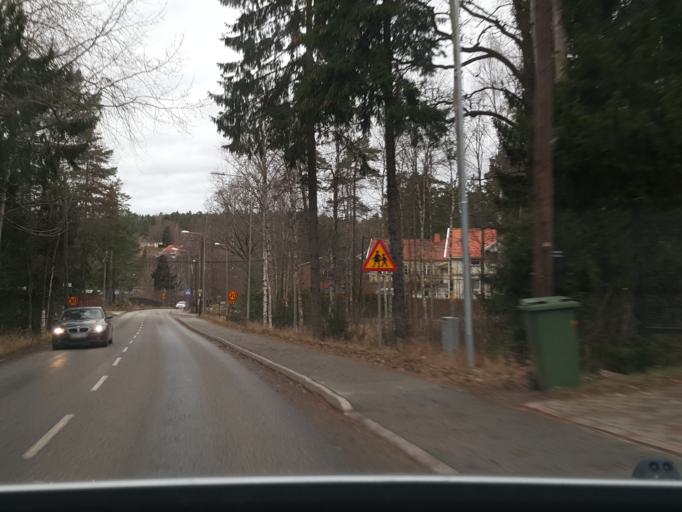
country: SE
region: Stockholm
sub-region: Nacka Kommun
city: Boo
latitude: 59.3266
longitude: 18.2862
